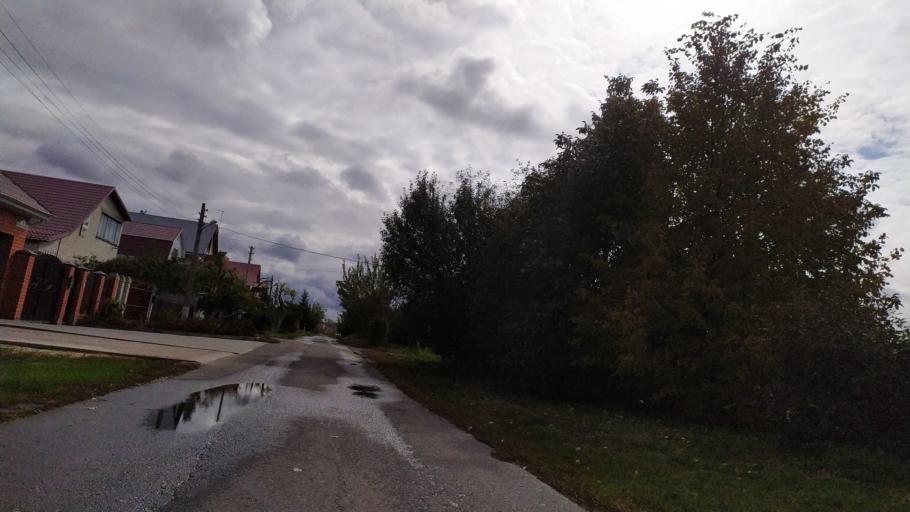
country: RU
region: Kursk
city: Kursk
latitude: 51.6439
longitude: 36.1541
